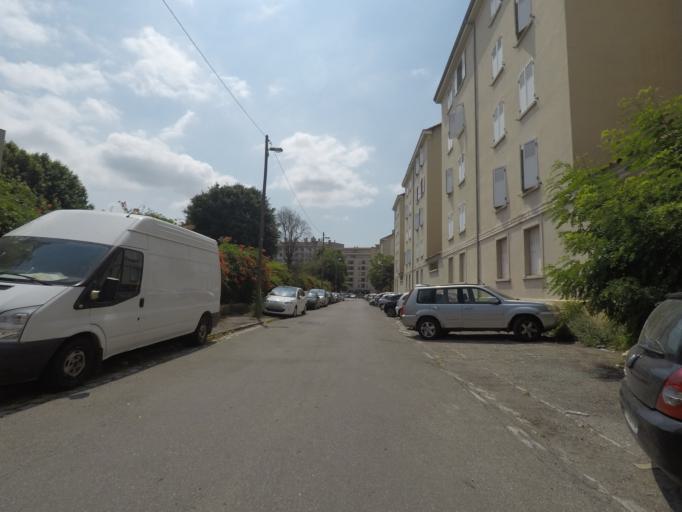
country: FR
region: Provence-Alpes-Cote d'Azur
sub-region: Departement des Bouches-du-Rhone
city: Marseille 10
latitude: 43.2840
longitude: 5.4078
